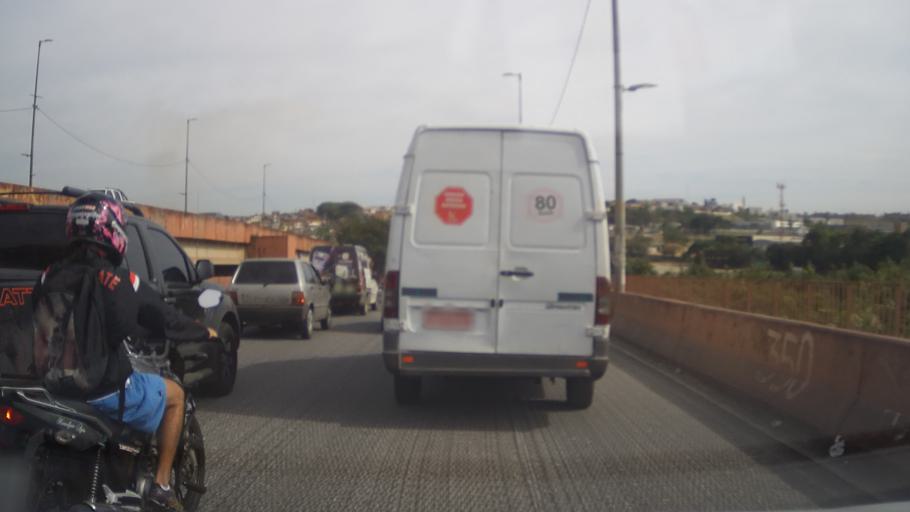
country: BR
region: Minas Gerais
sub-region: Contagem
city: Contagem
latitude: -19.9423
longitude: -44.0263
